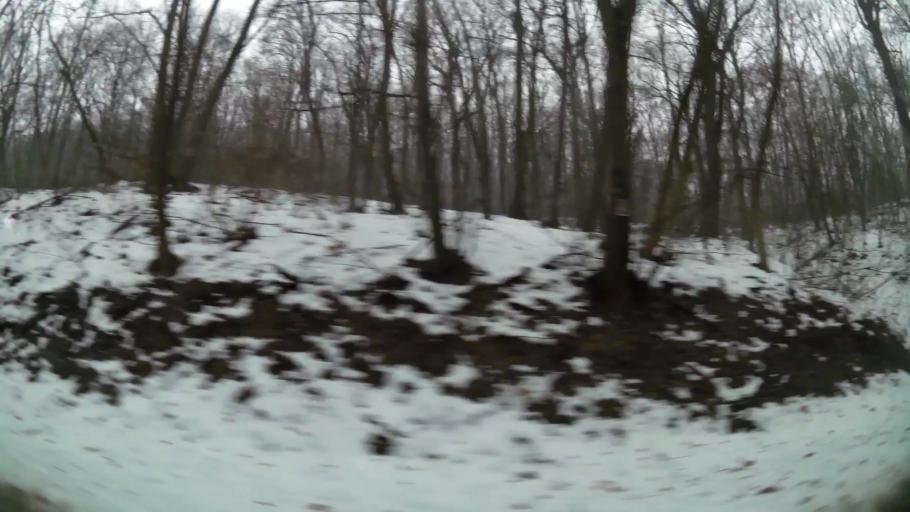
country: RS
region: Central Serbia
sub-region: Belgrade
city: Cukarica
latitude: 44.7730
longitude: 20.4349
